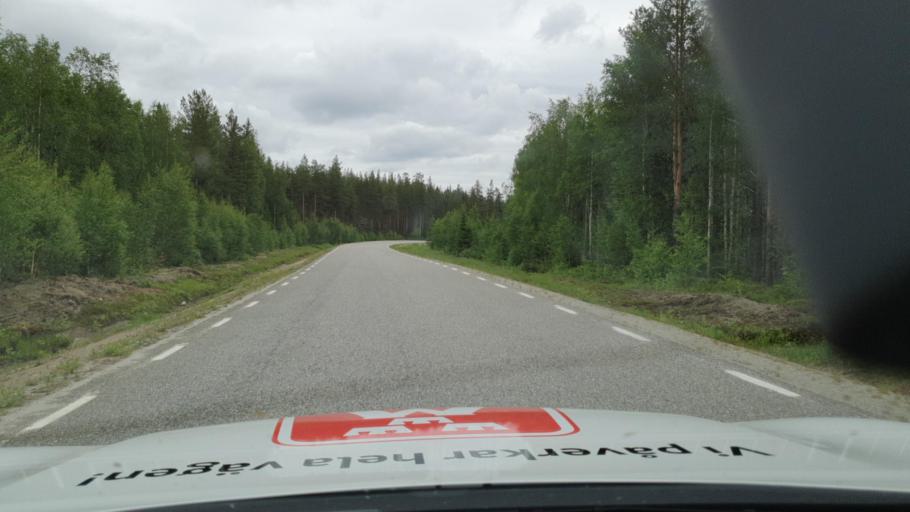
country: SE
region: Vaesterbotten
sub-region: Lycksele Kommun
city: Lycksele
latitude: 64.1943
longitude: 18.3038
